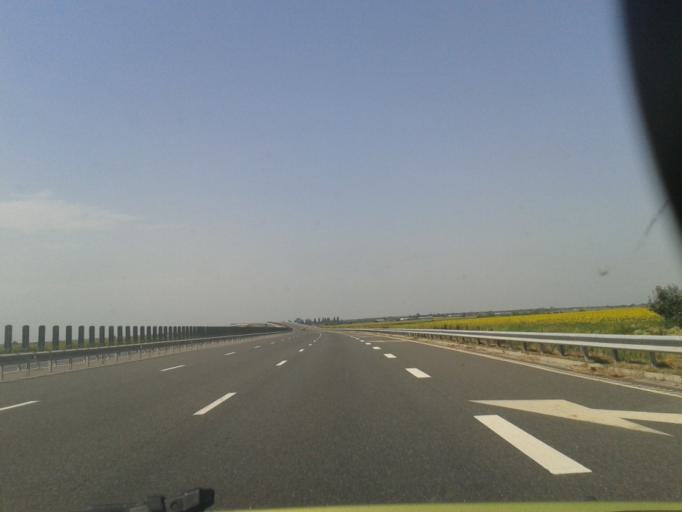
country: RO
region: Ilfov
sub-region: Comuna Moara Vlasiei
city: Caciulati
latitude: 44.6176
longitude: 26.1852
